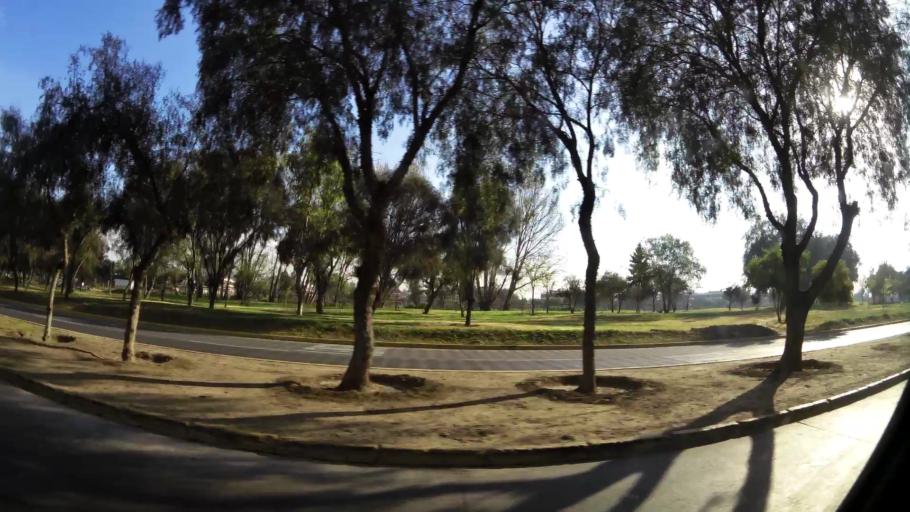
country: CL
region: Santiago Metropolitan
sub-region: Provincia de Santiago
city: Lo Prado
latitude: -33.4536
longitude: -70.7427
